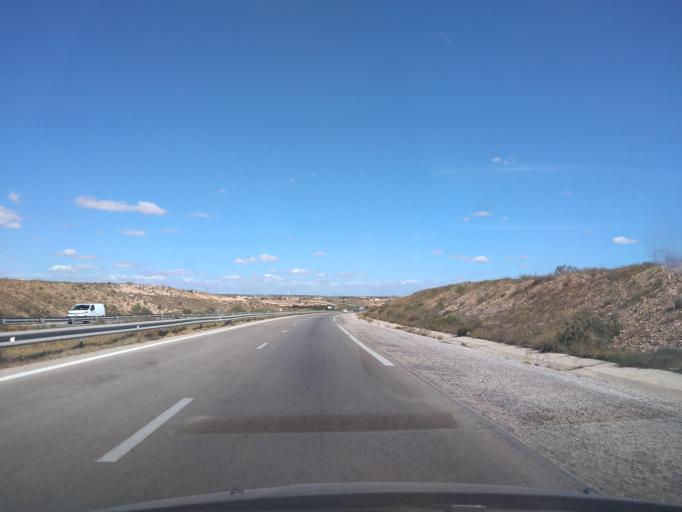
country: TN
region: Safaqis
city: Jabinyanah
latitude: 34.9502
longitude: 10.7357
